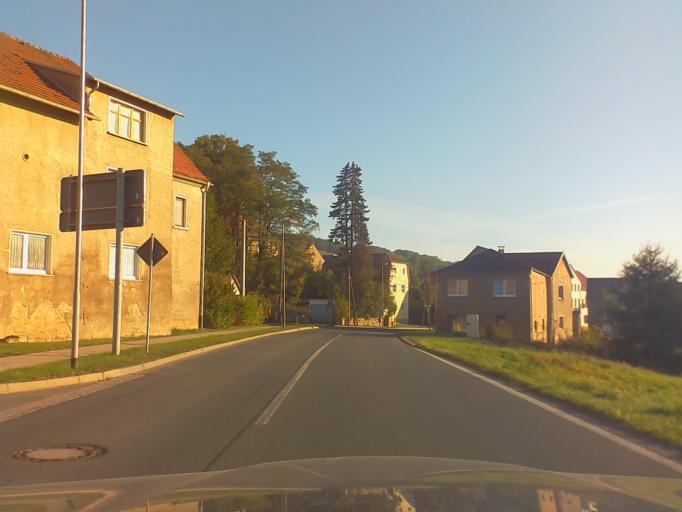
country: DE
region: Thuringia
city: Saara
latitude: 50.8562
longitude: 11.9760
